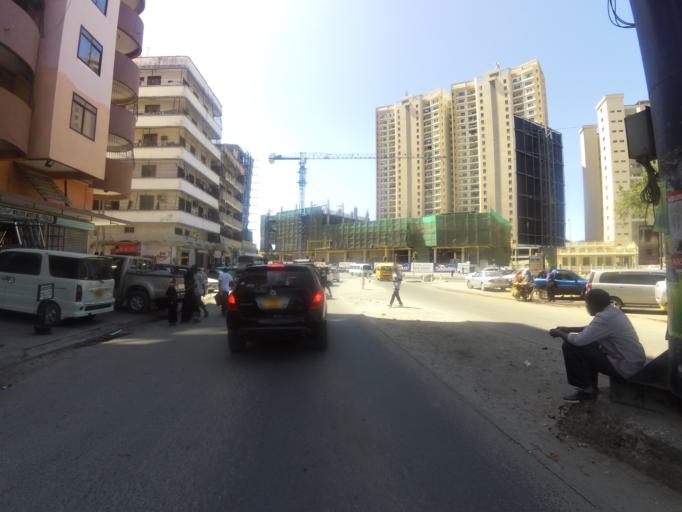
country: TZ
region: Dar es Salaam
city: Dar es Salaam
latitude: -6.8151
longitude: 39.2777
